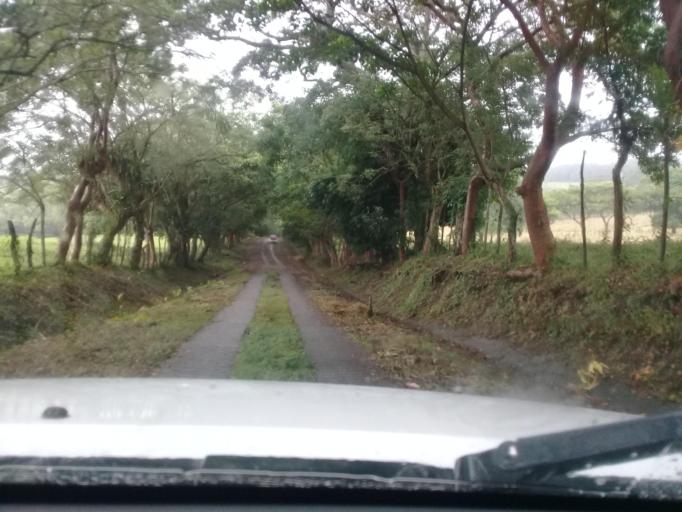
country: MX
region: Veracruz
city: Santiago Tuxtla
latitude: 18.4516
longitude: -95.2933
